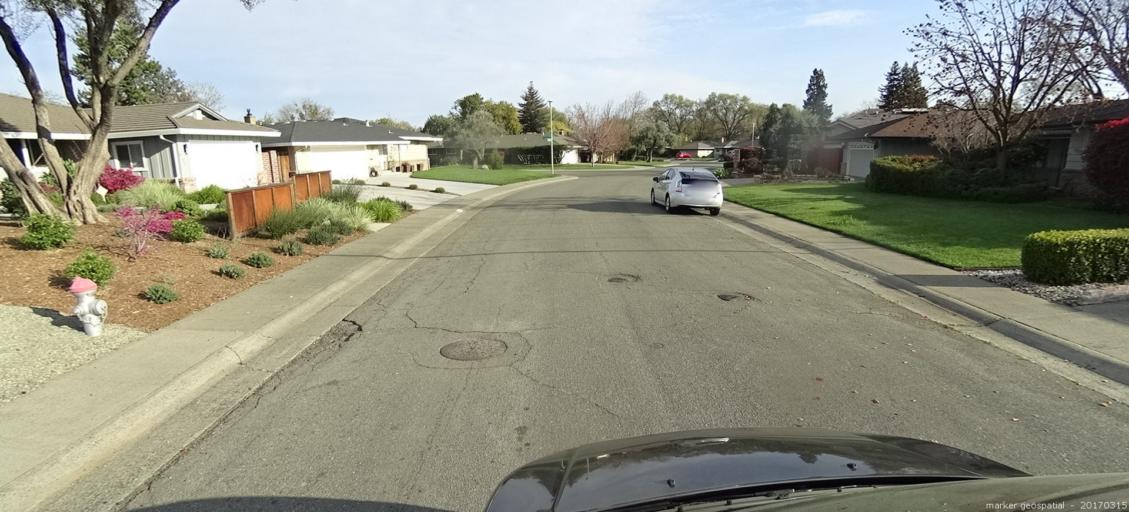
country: US
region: California
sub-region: Sacramento County
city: Parkway
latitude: 38.5030
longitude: -121.5112
